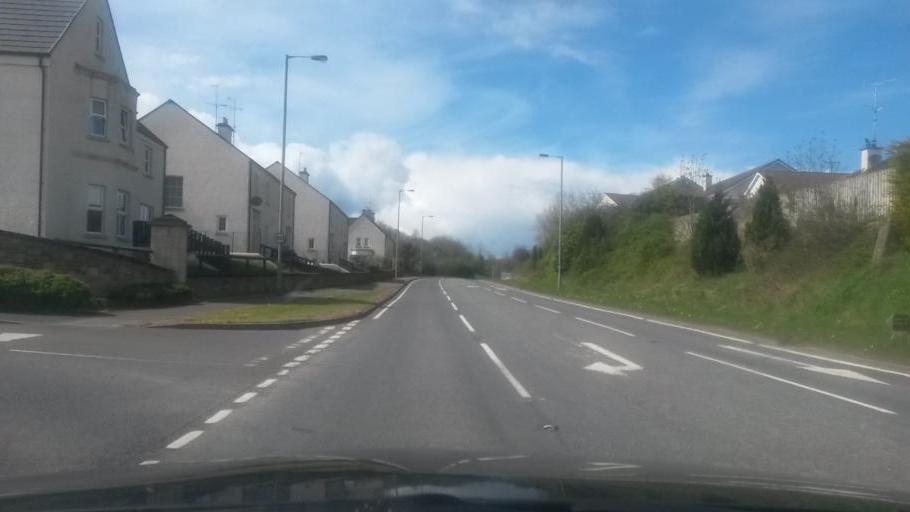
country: GB
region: Northern Ireland
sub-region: Fermanagh District
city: Enniskillen
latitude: 54.3613
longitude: -7.6755
